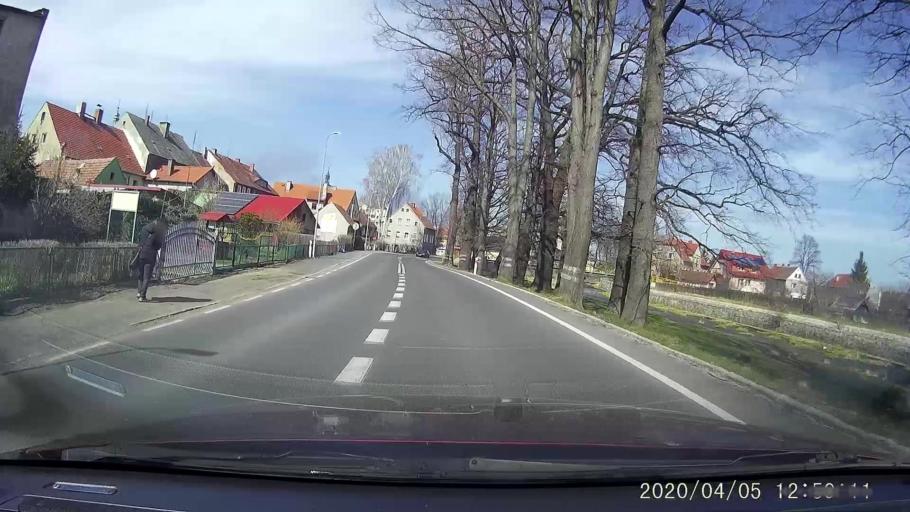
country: PL
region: Lower Silesian Voivodeship
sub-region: Powiat lwowecki
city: Mirsk
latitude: 50.9668
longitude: 15.3835
